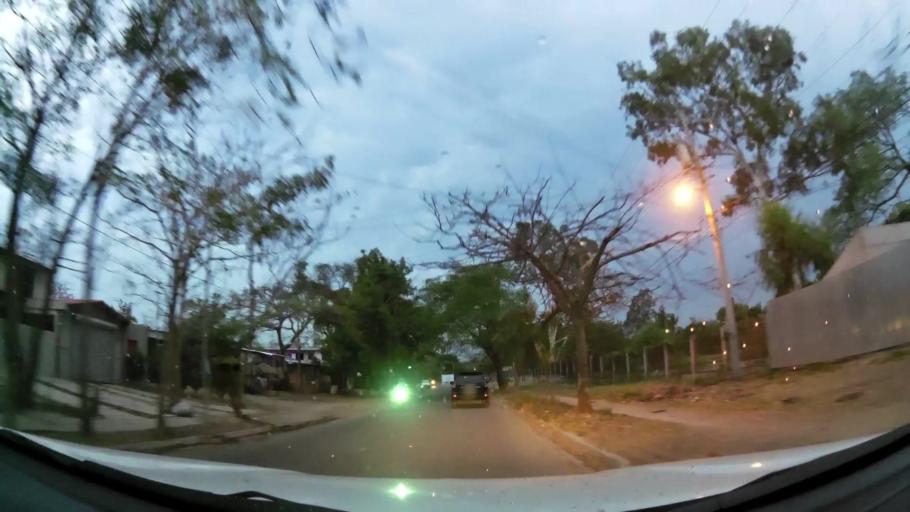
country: NI
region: Esteli
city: Esteli
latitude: 13.1042
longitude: -86.3584
